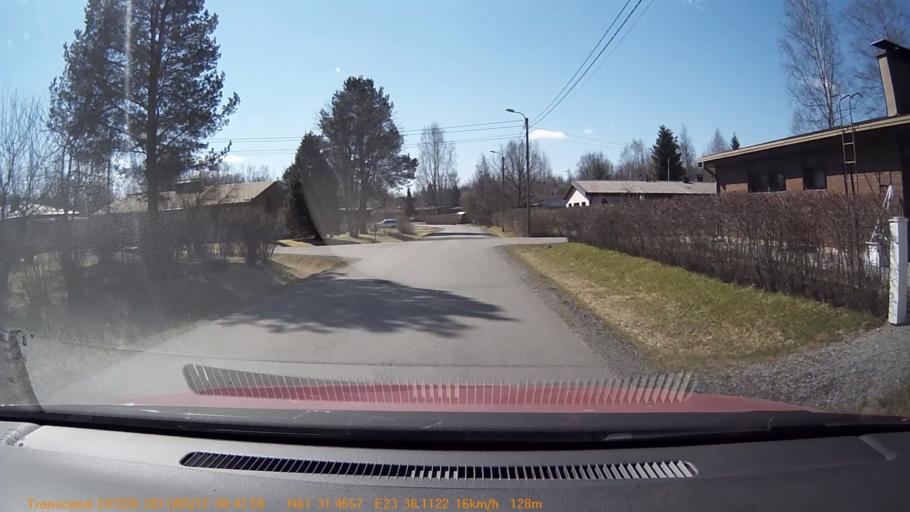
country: FI
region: Pirkanmaa
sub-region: Tampere
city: Yloejaervi
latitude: 61.5243
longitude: 23.6019
